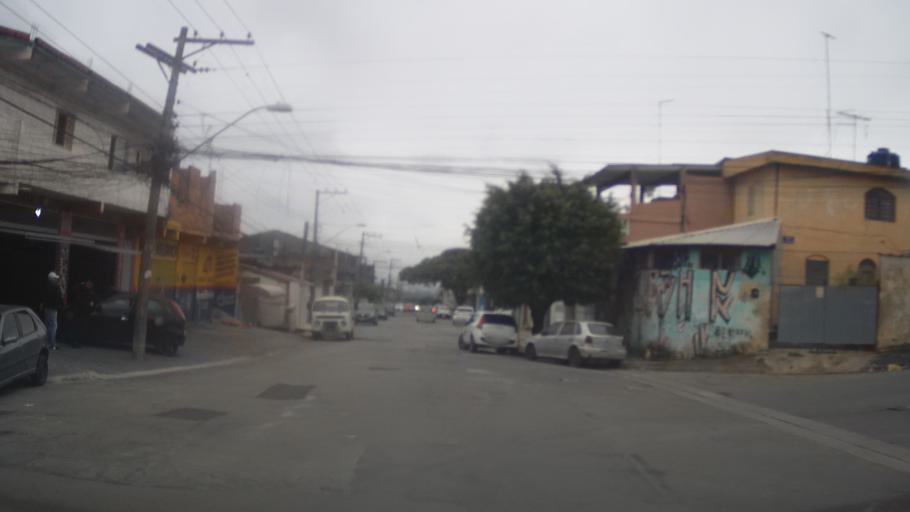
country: BR
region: Sao Paulo
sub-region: Guarulhos
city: Guarulhos
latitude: -23.4315
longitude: -46.5139
